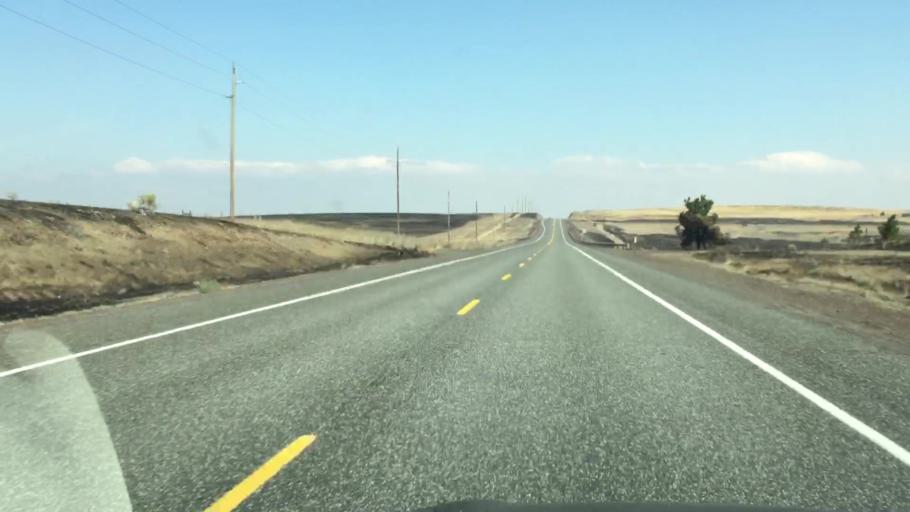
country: US
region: Oregon
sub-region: Wasco County
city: The Dalles
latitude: 45.3511
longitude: -121.1421
